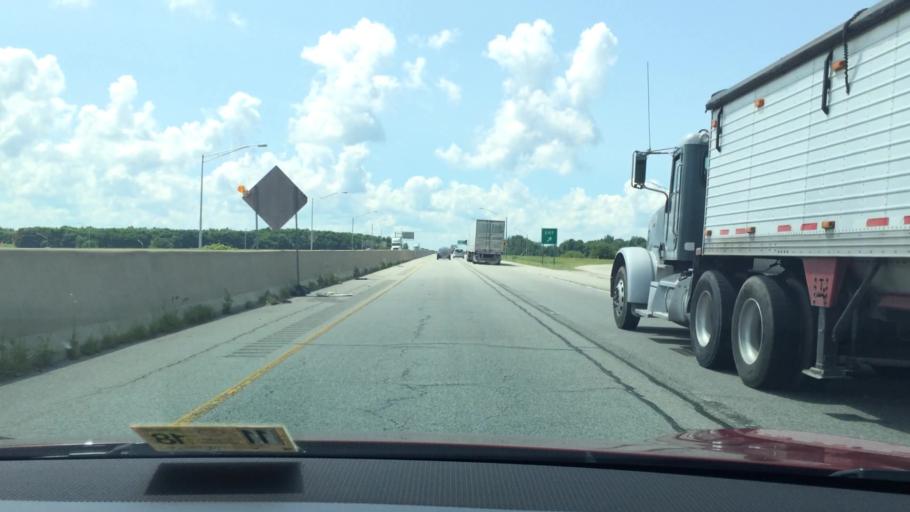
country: US
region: Indiana
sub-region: Saint Joseph County
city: South Bend
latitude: 41.7099
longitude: -86.3399
